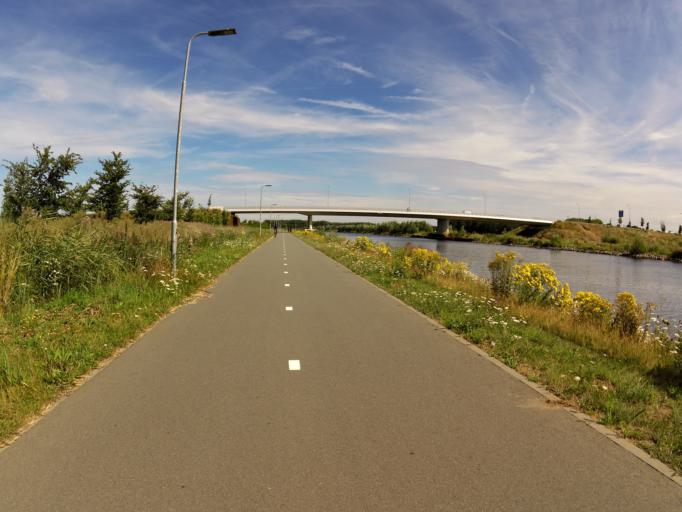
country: NL
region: North Brabant
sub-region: Gemeente 's-Hertogenbosch
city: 's-Hertogenbosch
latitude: 51.7256
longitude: 5.3397
